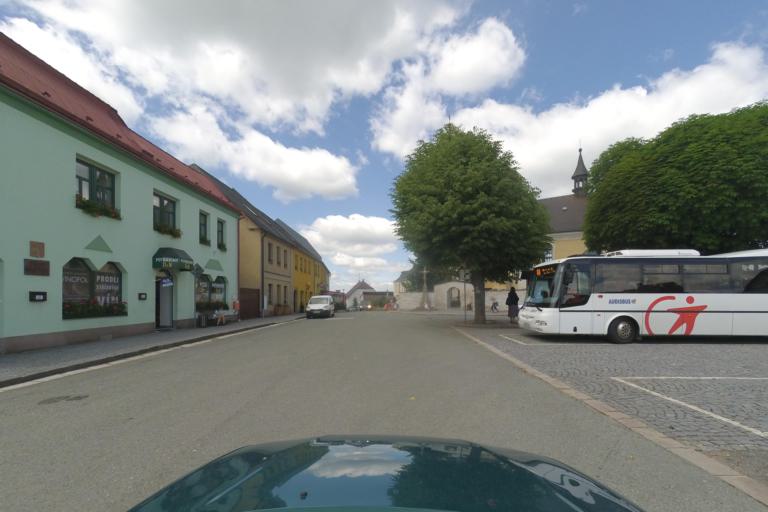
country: PL
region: Lower Silesian Voivodeship
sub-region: Powiat klodzki
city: Lewin Klodzki
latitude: 50.3576
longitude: 16.2437
